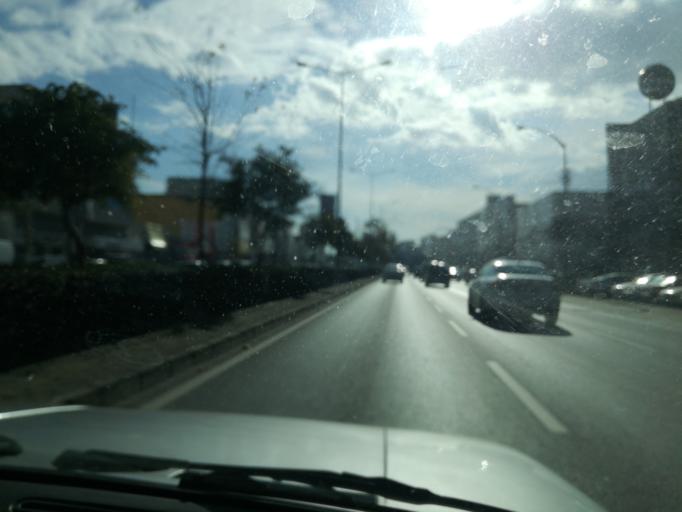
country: TR
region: Izmir
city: Karabaglar
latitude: 38.3759
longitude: 27.1349
